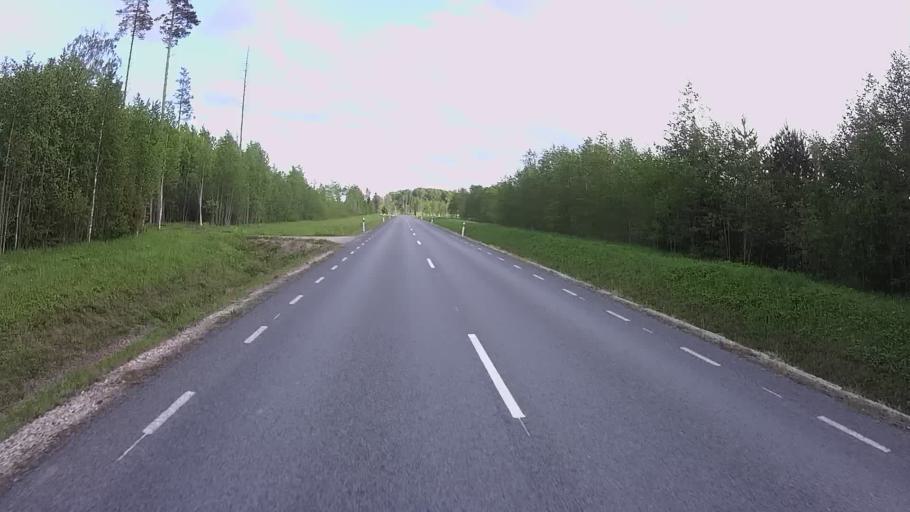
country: EE
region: Jogevamaa
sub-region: Mustvee linn
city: Mustvee
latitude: 59.0570
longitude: 27.0099
